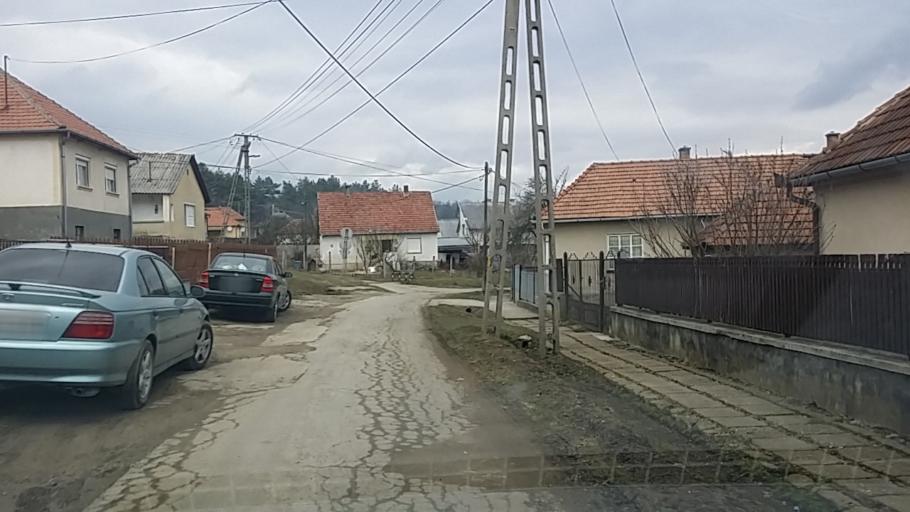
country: HU
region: Borsod-Abauj-Zemplen
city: Rudabanya
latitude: 48.3825
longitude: 20.6233
